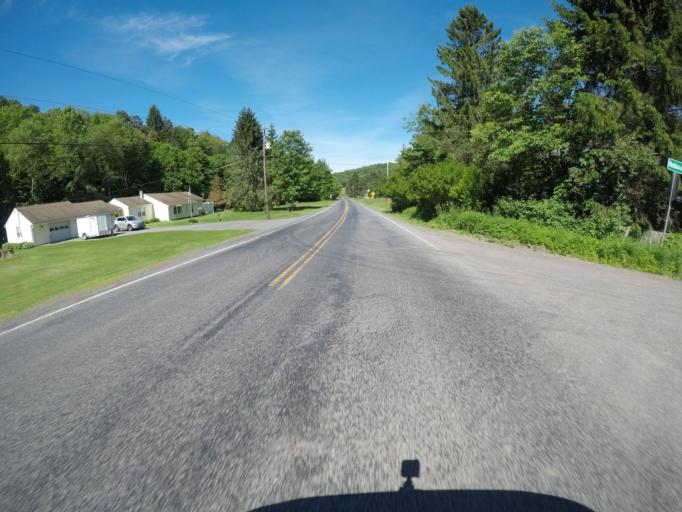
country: US
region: New York
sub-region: Delaware County
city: Delhi
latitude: 42.2170
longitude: -74.8839
